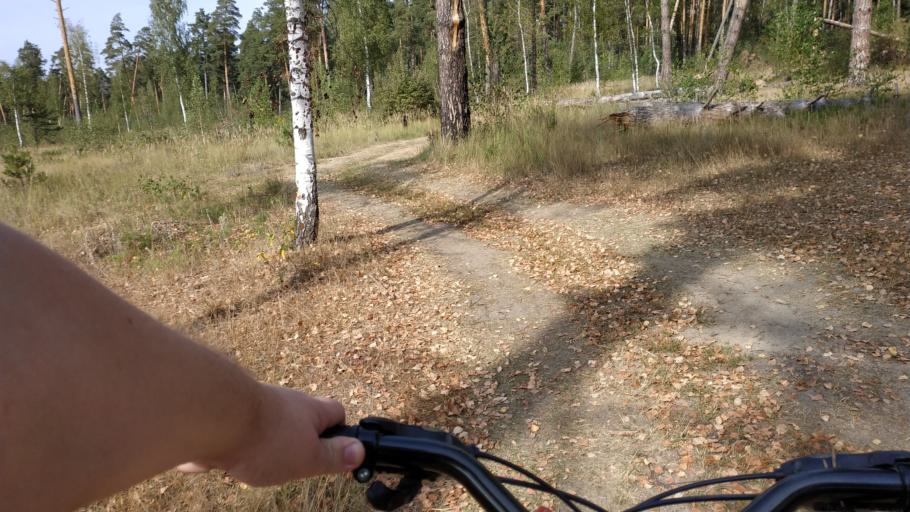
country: RU
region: Moskovskaya
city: Ramenskoye
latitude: 55.5327
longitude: 38.2929
